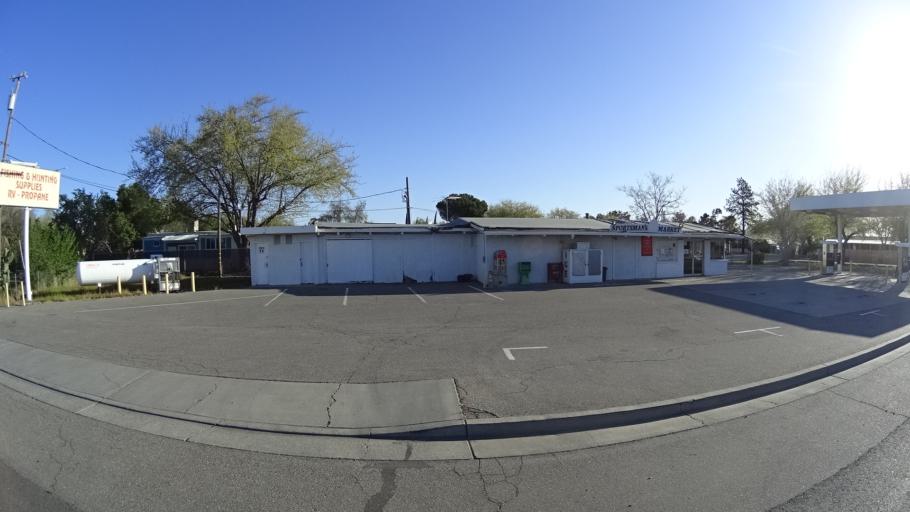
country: US
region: California
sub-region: Glenn County
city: Orland
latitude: 39.7527
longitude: -122.2105
